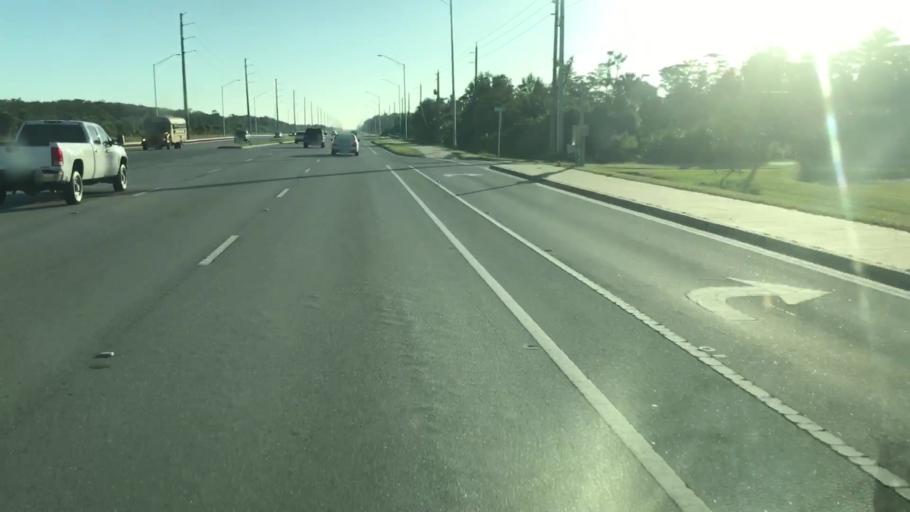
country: US
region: Florida
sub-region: Collier County
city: Orangetree
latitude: 26.2736
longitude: -81.6496
